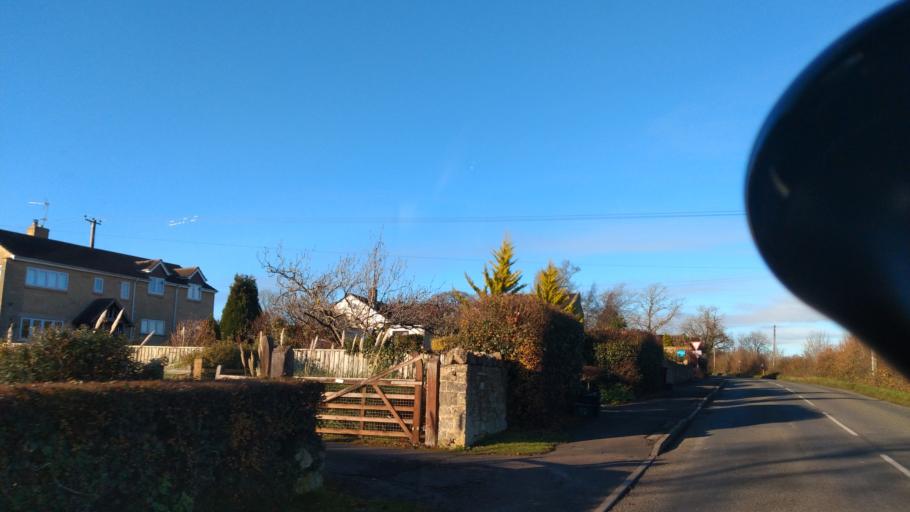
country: GB
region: England
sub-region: Wiltshire
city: Wingfield
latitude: 51.2839
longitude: -2.2741
